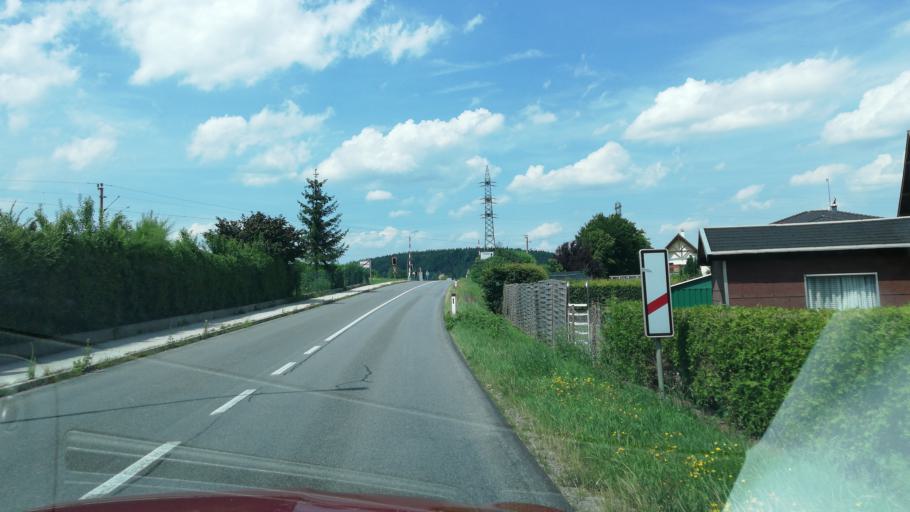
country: AT
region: Upper Austria
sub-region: Politischer Bezirk Vocklabruck
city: Timelkam
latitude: 47.9936
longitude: 13.6150
